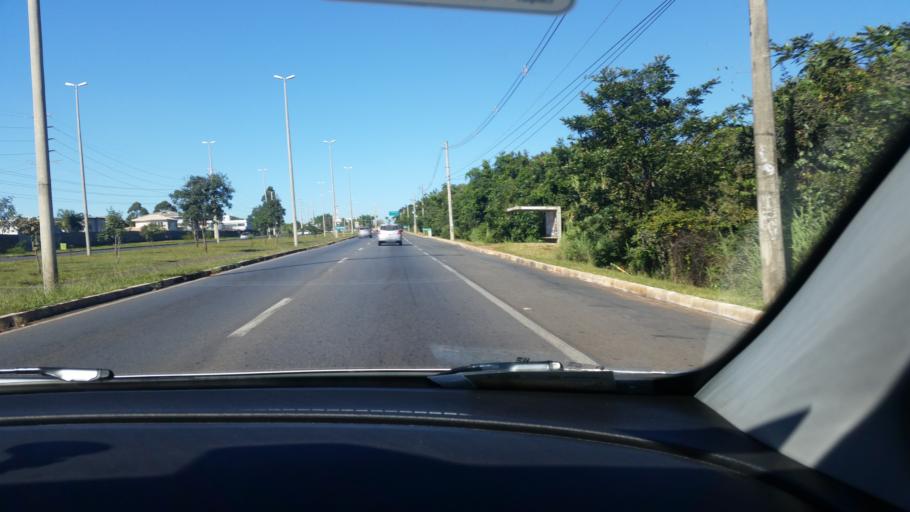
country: BR
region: Federal District
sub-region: Brasilia
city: Brasilia
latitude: -15.8588
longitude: -47.8187
